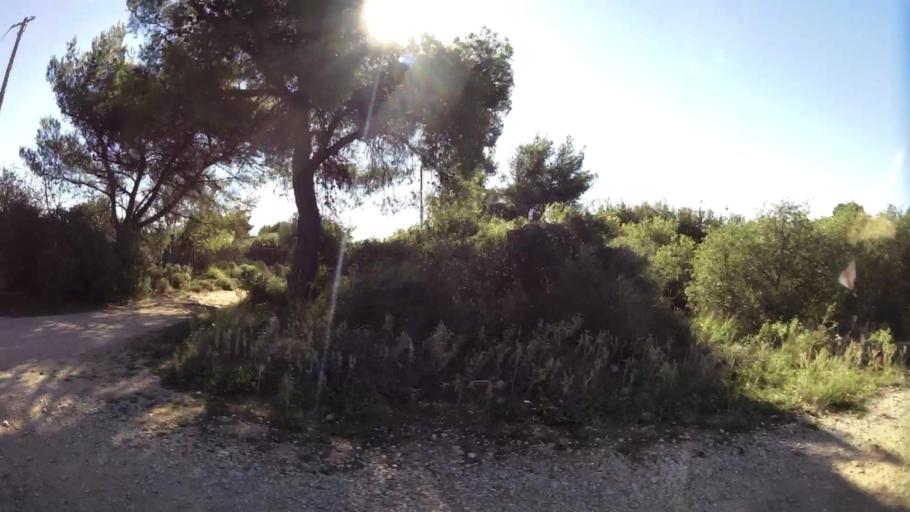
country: GR
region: Attica
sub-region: Nomarchia Anatolikis Attikis
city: Varybobi
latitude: 38.1232
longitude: 23.7834
